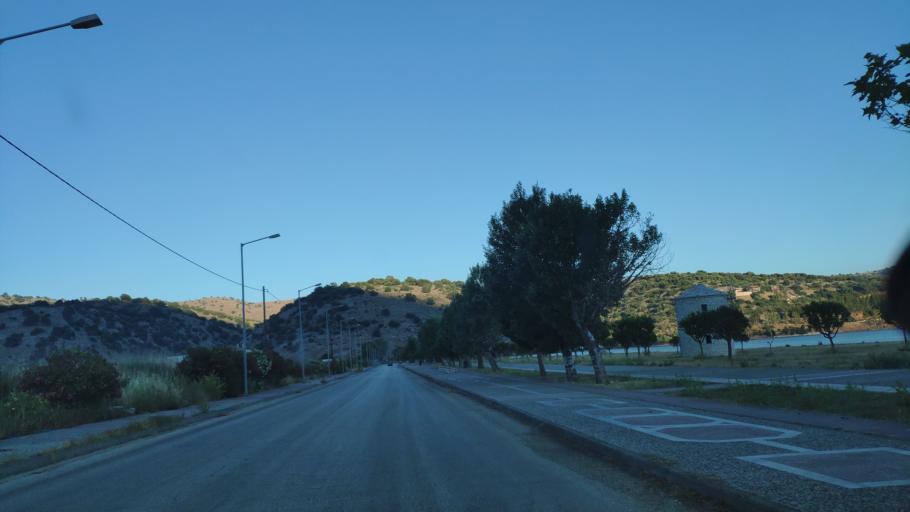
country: GR
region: West Greece
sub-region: Nomos Aitolias kai Akarnanias
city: Astakos
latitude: 38.5345
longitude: 21.0914
